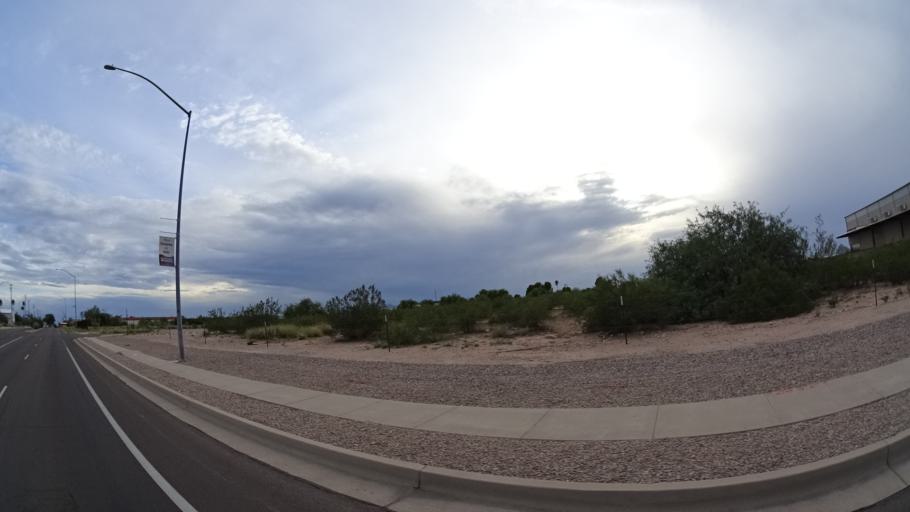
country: US
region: Arizona
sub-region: Pima County
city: South Tucson
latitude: 32.1384
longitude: -110.9348
